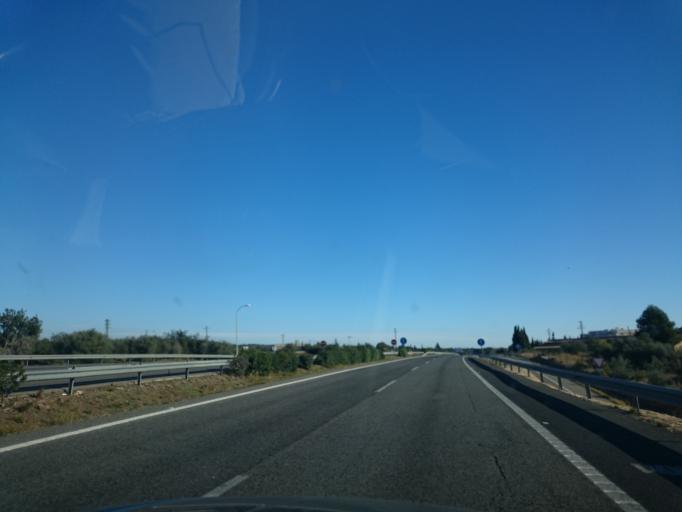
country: ES
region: Catalonia
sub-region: Provincia de Tarragona
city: L'Ampolla
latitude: 40.8121
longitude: 0.7024
